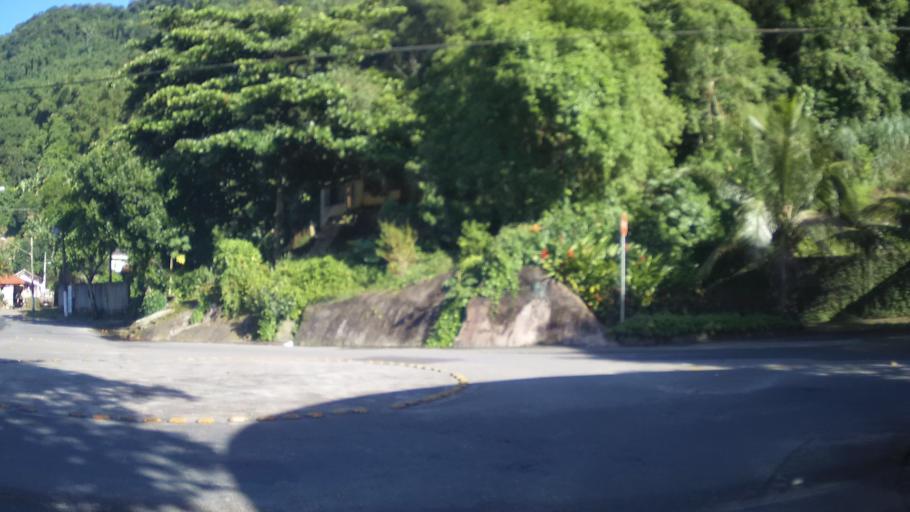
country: BR
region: Sao Paulo
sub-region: Santos
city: Santos
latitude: -23.9505
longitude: -46.3456
